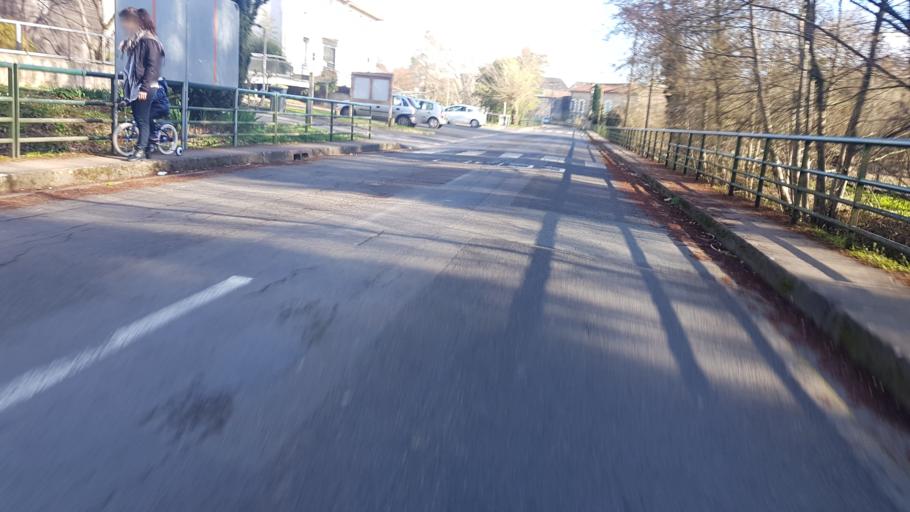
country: FR
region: Poitou-Charentes
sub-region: Departement de la Vienne
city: Migne-Auxances
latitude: 46.6276
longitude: 0.3088
